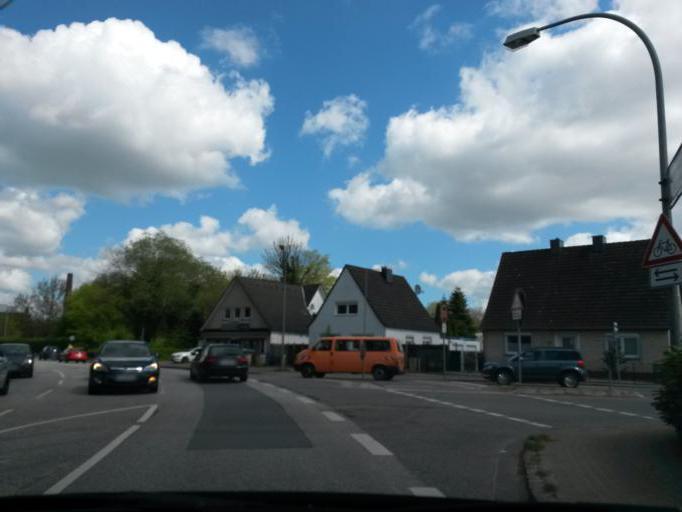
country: DE
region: Schleswig-Holstein
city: Moorrege
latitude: 53.6760
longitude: 9.6770
